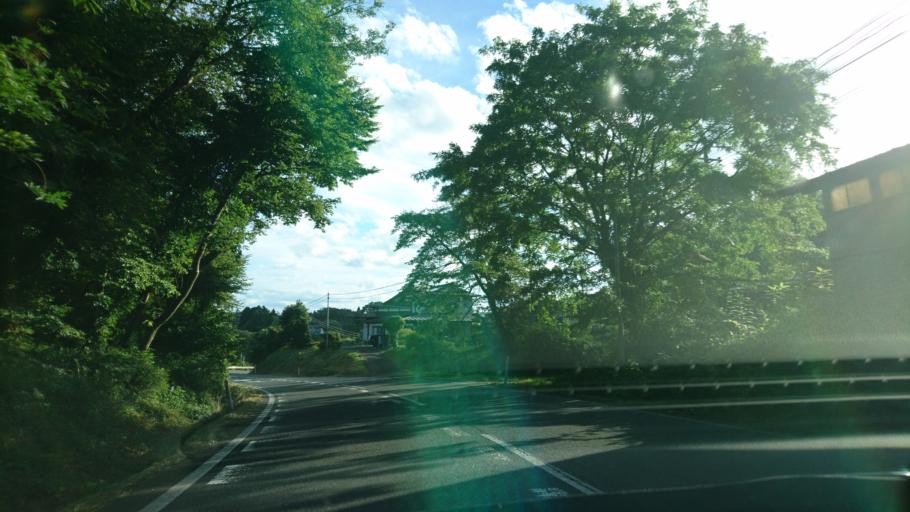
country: JP
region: Iwate
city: Ichinoseki
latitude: 38.8812
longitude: 141.2172
